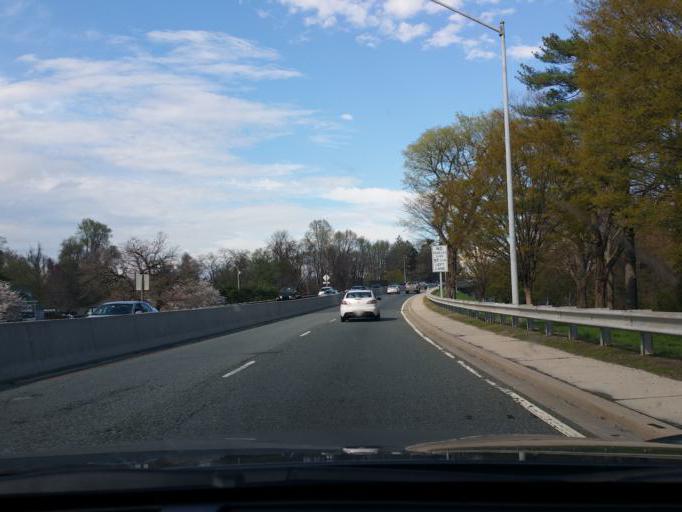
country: US
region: Maryland
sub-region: Harford County
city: Havre de Grace
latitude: 39.5554
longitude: -76.0998
